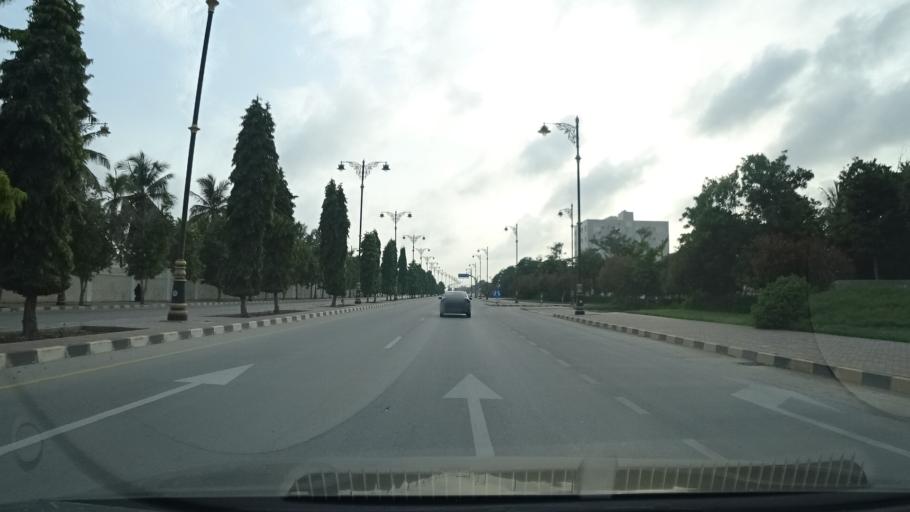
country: OM
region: Zufar
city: Salalah
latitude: 17.0261
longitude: 54.1633
